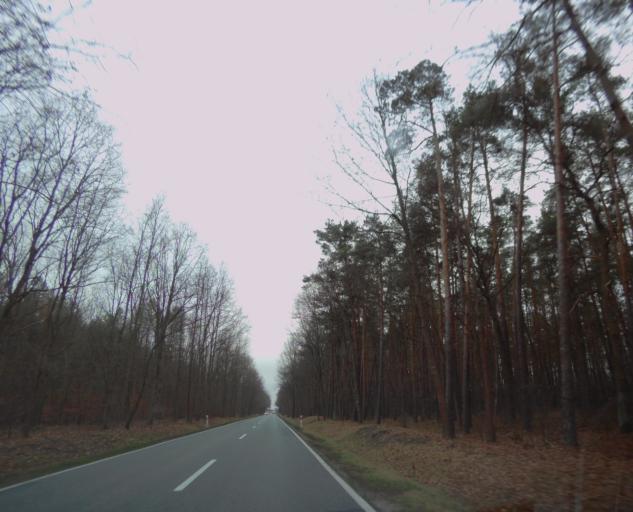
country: PL
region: Subcarpathian Voivodeship
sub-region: Powiat nizanski
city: Krzeszow
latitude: 50.3941
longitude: 22.3002
